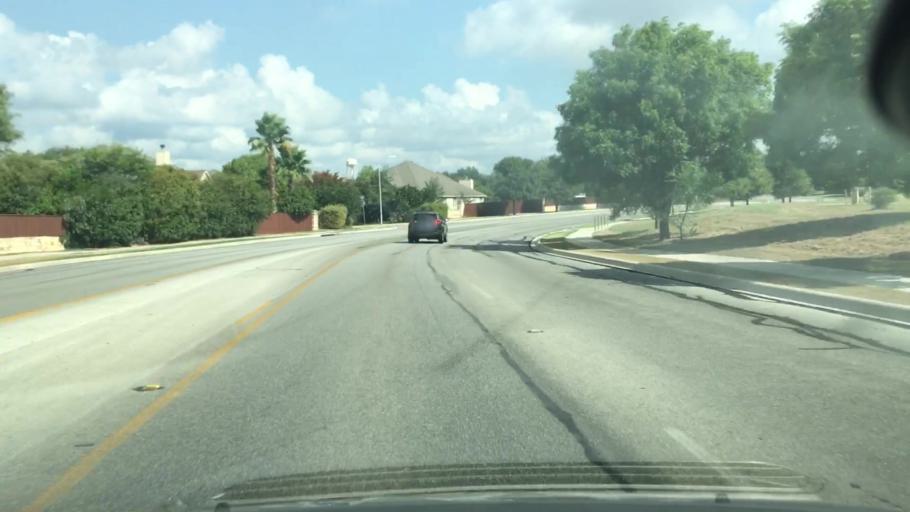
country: US
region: Texas
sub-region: Guadalupe County
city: Cibolo
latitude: 29.5884
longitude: -98.2490
